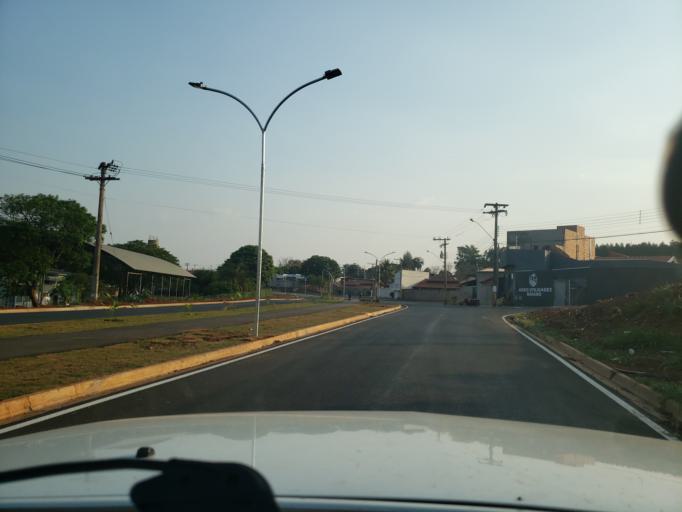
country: BR
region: Sao Paulo
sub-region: Moji-Guacu
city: Mogi-Gaucu
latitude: -22.3254
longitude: -46.9501
